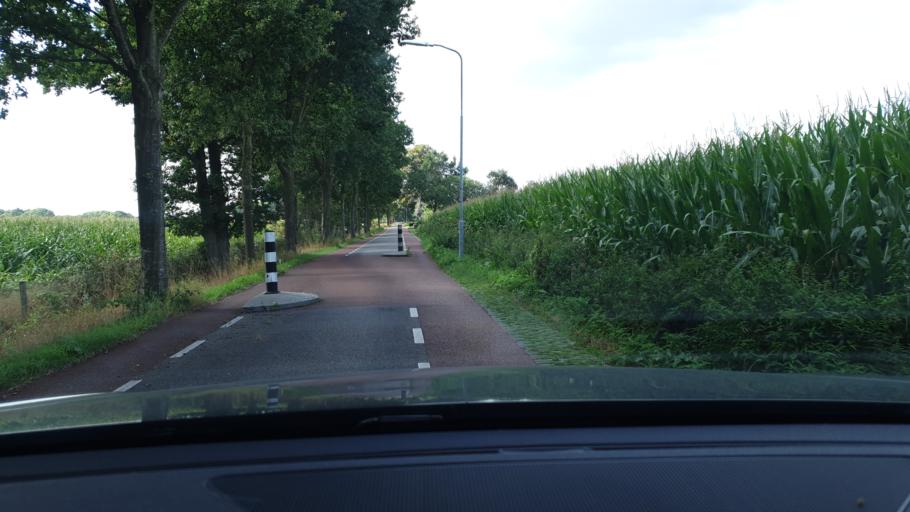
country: NL
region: Gelderland
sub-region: Gemeente Groesbeek
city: De Horst
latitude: 51.7817
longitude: 5.9879
